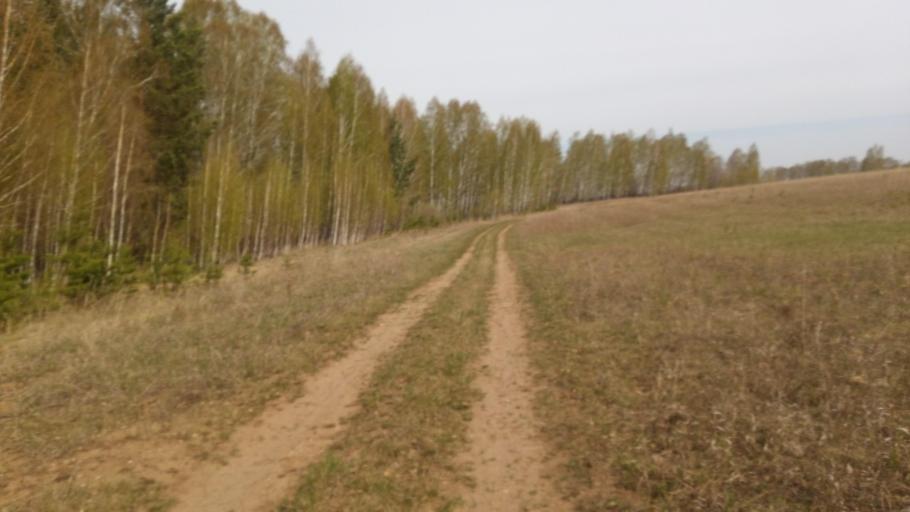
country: RU
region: Chelyabinsk
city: Timiryazevskiy
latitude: 55.0211
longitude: 60.8591
